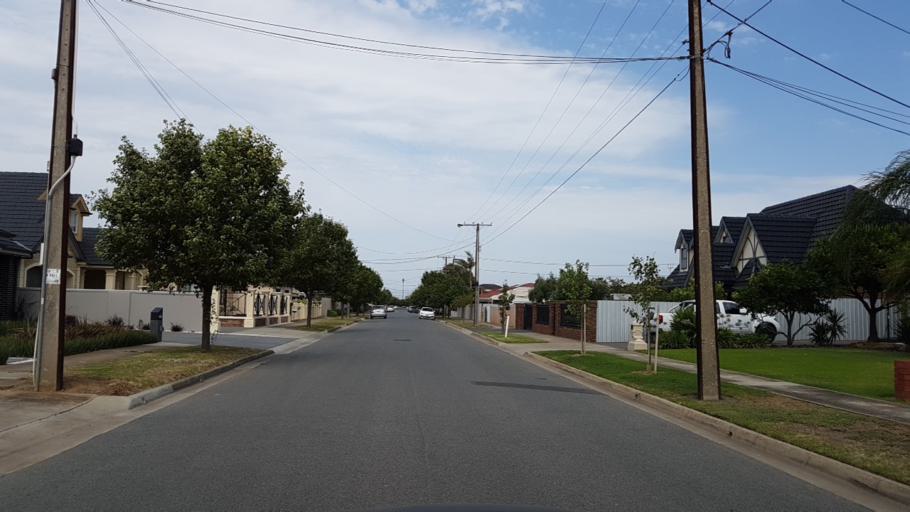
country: AU
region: South Australia
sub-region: Charles Sturt
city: Henley Beach
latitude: -34.9121
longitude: 138.5061
